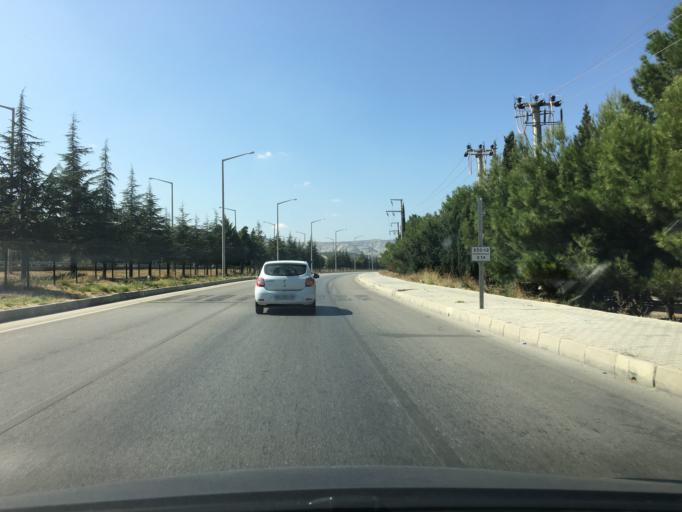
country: TR
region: Burdur
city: Burdur
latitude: 37.7336
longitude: 30.3095
